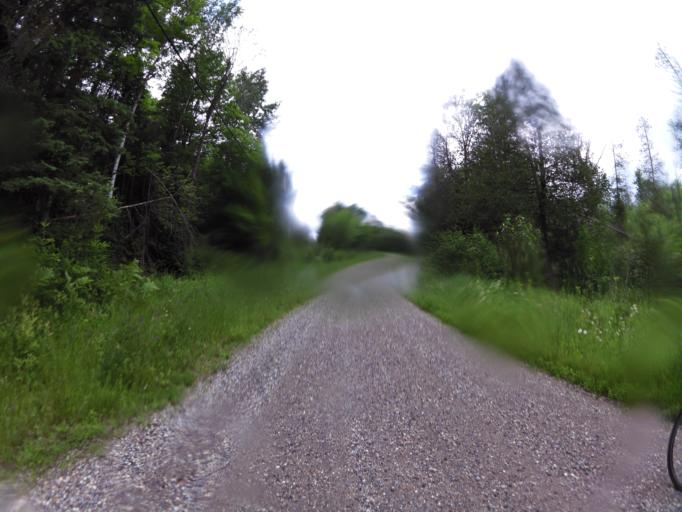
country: CA
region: Ontario
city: Renfrew
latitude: 45.0707
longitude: -76.7527
